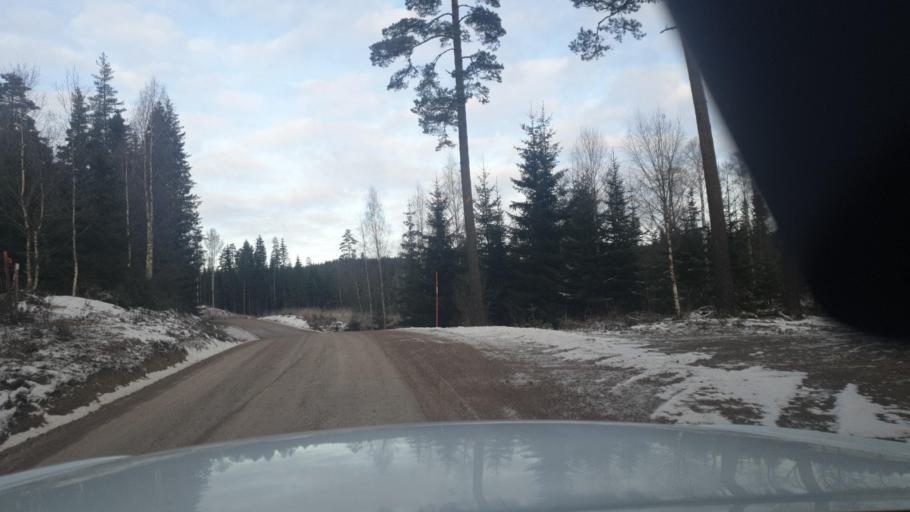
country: SE
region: Vaermland
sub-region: Arvika Kommun
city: Arvika
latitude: 59.9476
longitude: 12.6615
